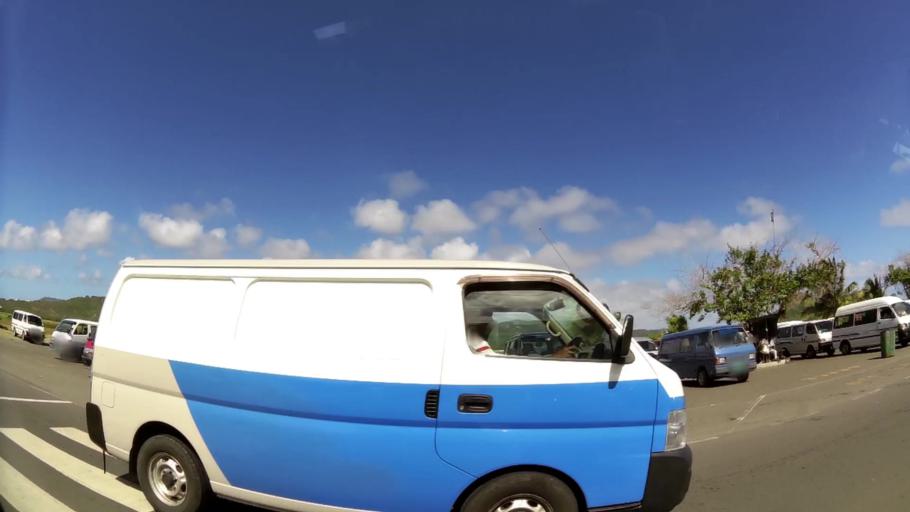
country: LC
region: Vieux-Fort
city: Vieux Fort
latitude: 13.7315
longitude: -60.9532
